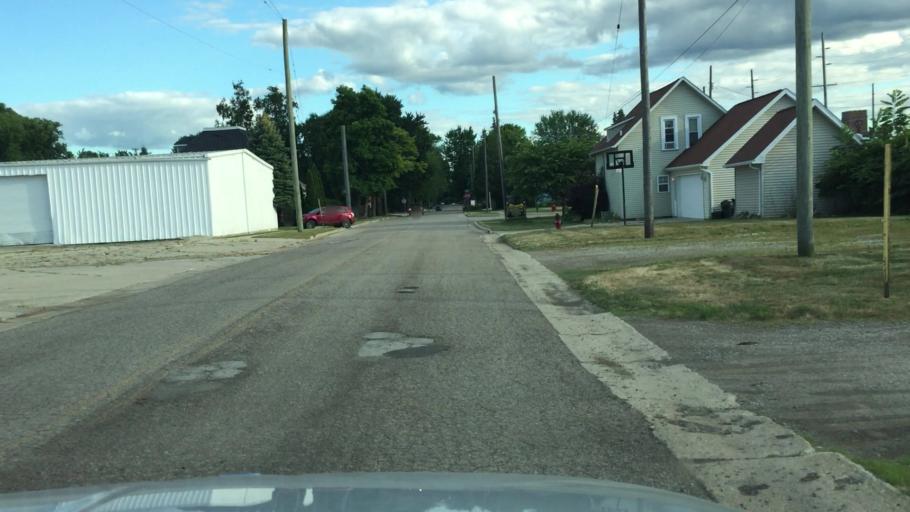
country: US
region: Michigan
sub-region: Saint Clair County
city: Yale
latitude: 43.1316
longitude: -82.7972
